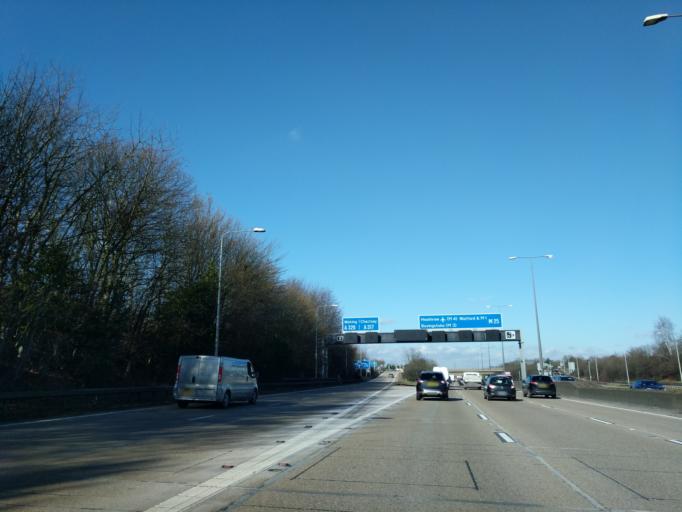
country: GB
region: England
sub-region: Surrey
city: Addlestone
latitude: 51.3715
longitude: -0.5076
